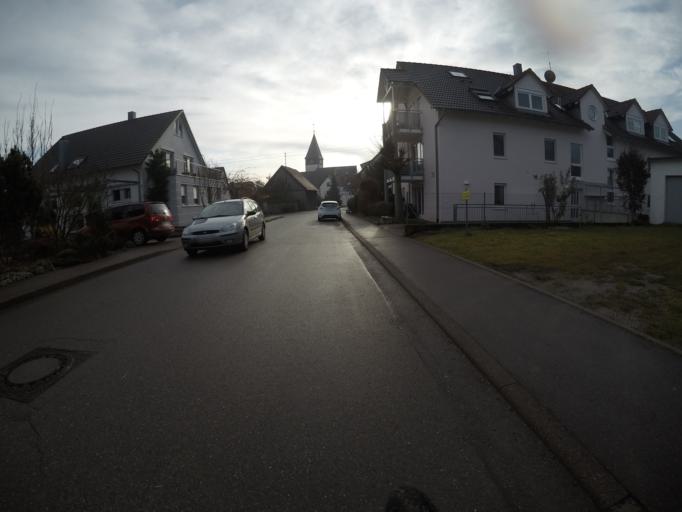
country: DE
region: Baden-Wuerttemberg
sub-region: Regierungsbezirk Stuttgart
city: Herrenberg
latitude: 48.6132
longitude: 8.8387
